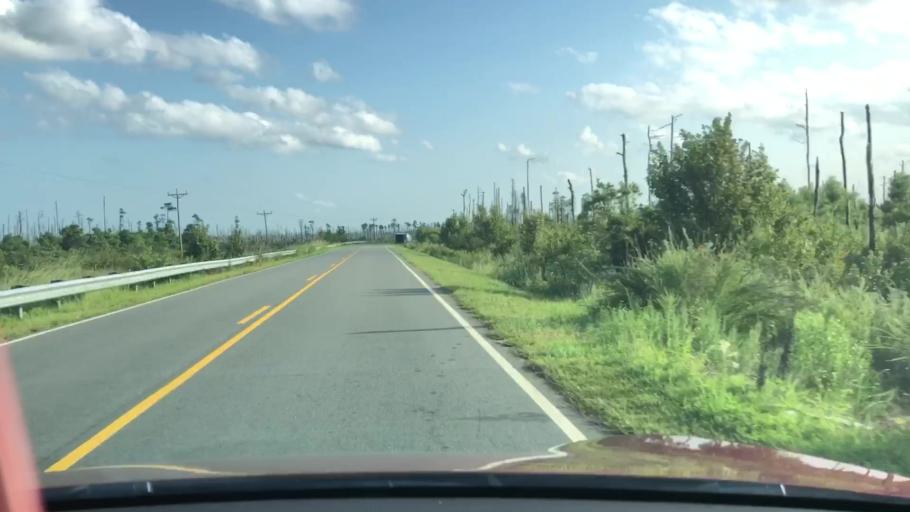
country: US
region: North Carolina
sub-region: Dare County
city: Wanchese
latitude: 35.6455
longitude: -75.7772
